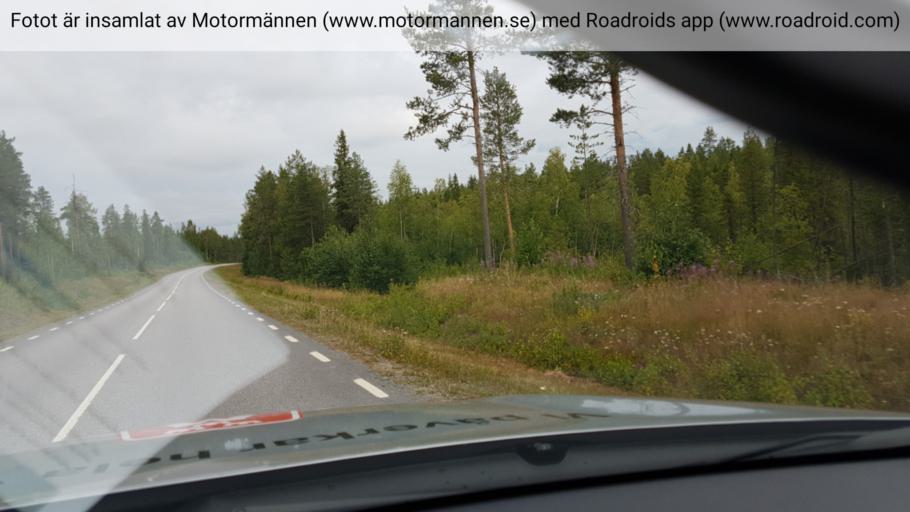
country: SE
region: Norrbotten
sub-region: Bodens Kommun
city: Saevast
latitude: 65.6772
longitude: 21.6493
